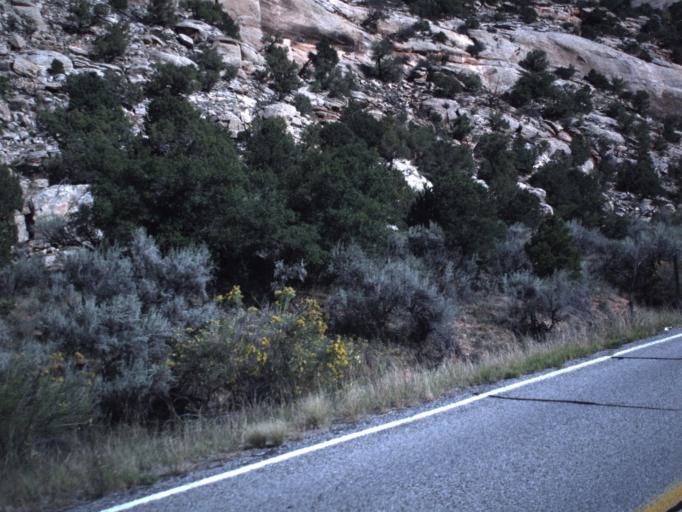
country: US
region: Utah
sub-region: San Juan County
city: Monticello
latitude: 38.0155
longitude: -109.5386
